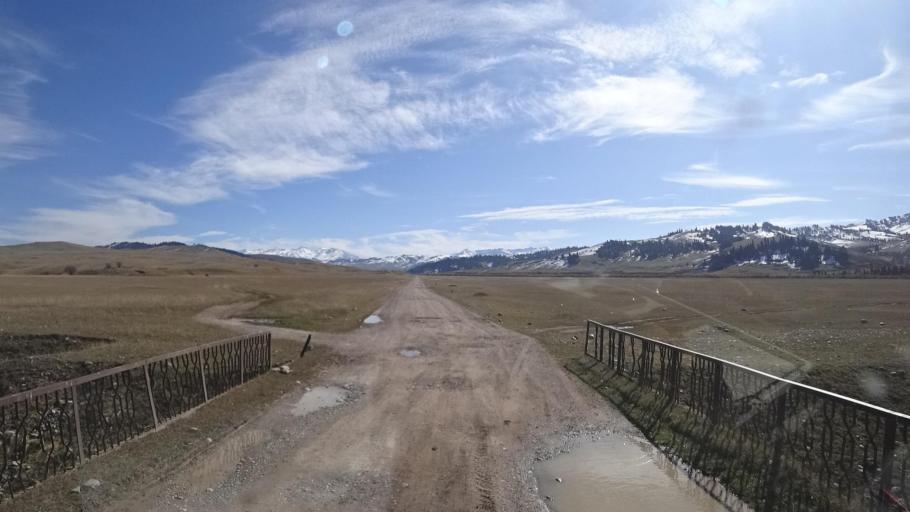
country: KZ
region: Almaty Oblysy
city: Kegen
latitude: 42.7471
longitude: 78.9908
